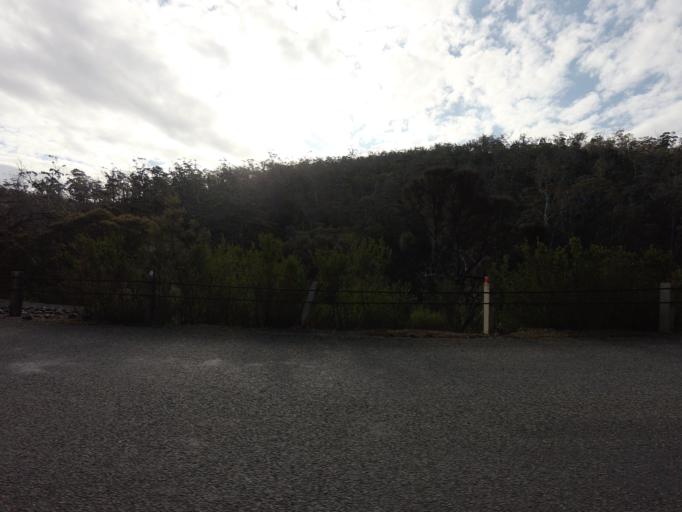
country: AU
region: Tasmania
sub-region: Sorell
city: Sorell
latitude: -42.5574
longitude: 147.8282
